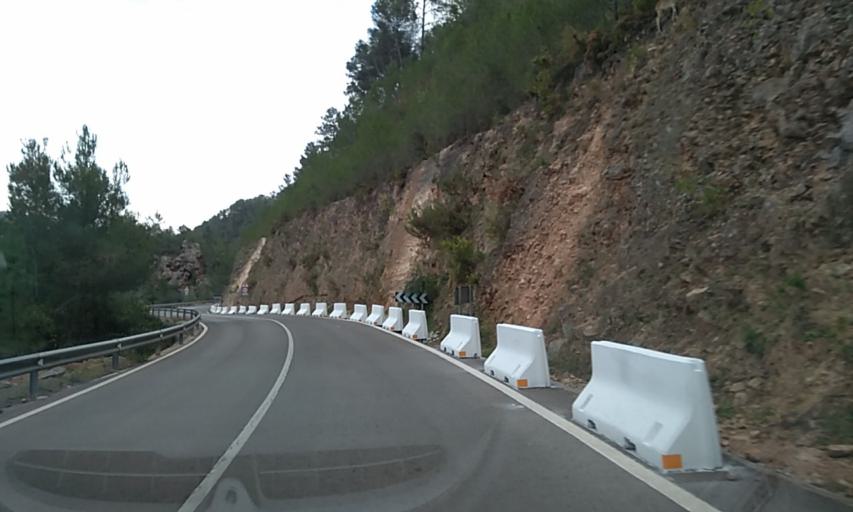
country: ES
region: Valencia
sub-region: Provincia de Castello
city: Montanejos
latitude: 40.0746
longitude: -0.5375
